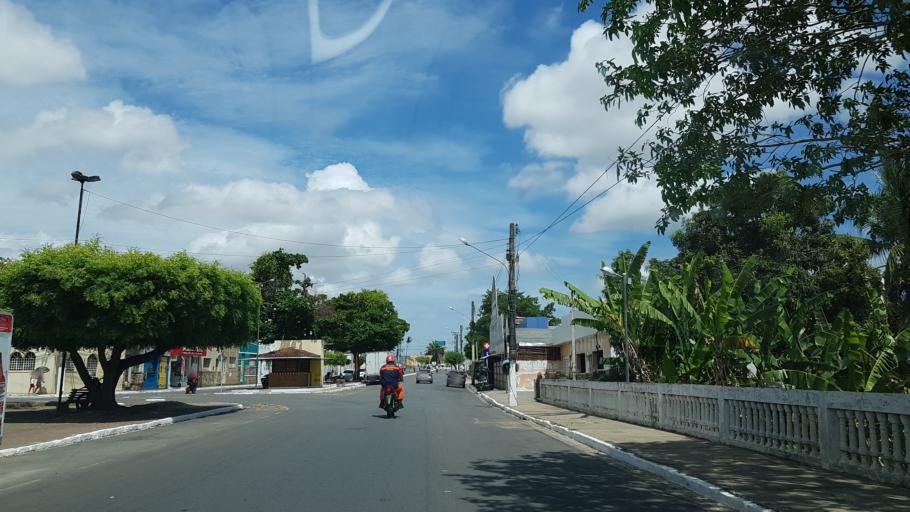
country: BR
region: Alagoas
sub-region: Penedo
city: Penedo
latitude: -10.2834
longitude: -36.5698
